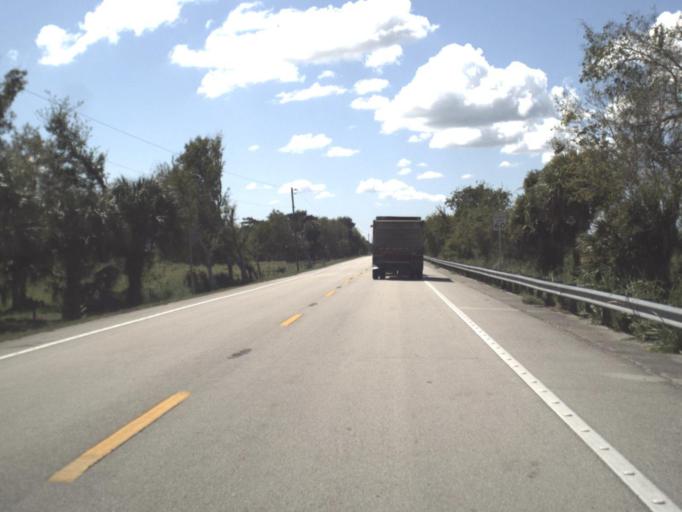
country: US
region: Florida
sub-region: Glades County
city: Buckhead Ridge
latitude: 27.1275
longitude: -80.9083
